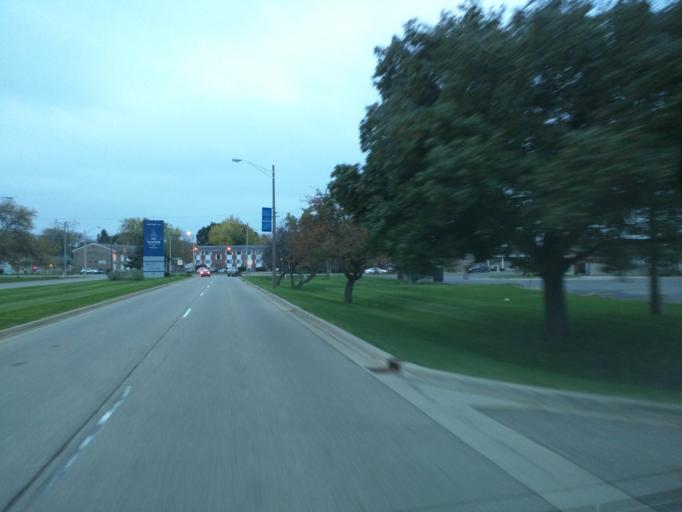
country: US
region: Michigan
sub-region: Ingham County
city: Edgemont Park
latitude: 42.7674
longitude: -84.5891
